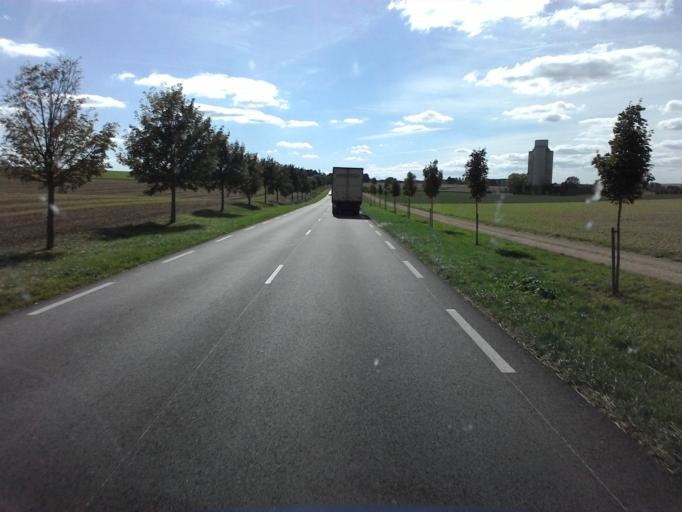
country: FR
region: Bourgogne
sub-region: Departement de la Cote-d'Or
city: Chatillon-sur-Seine
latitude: 47.7371
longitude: 4.4761
